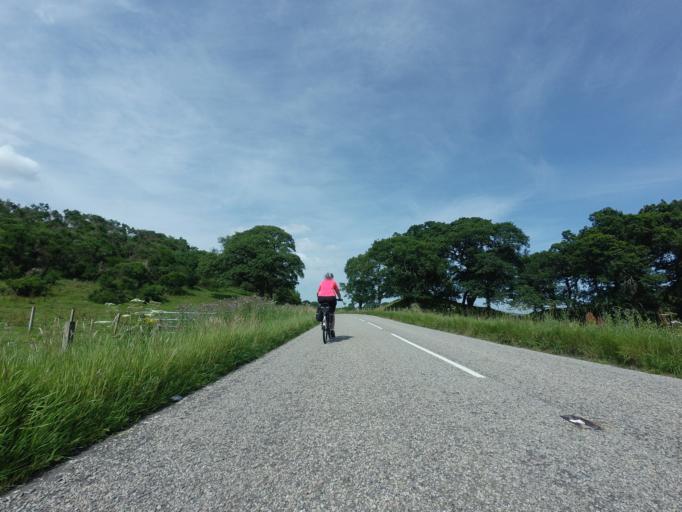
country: GB
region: Scotland
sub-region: Highland
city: Tain
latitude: 57.8507
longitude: -4.2037
